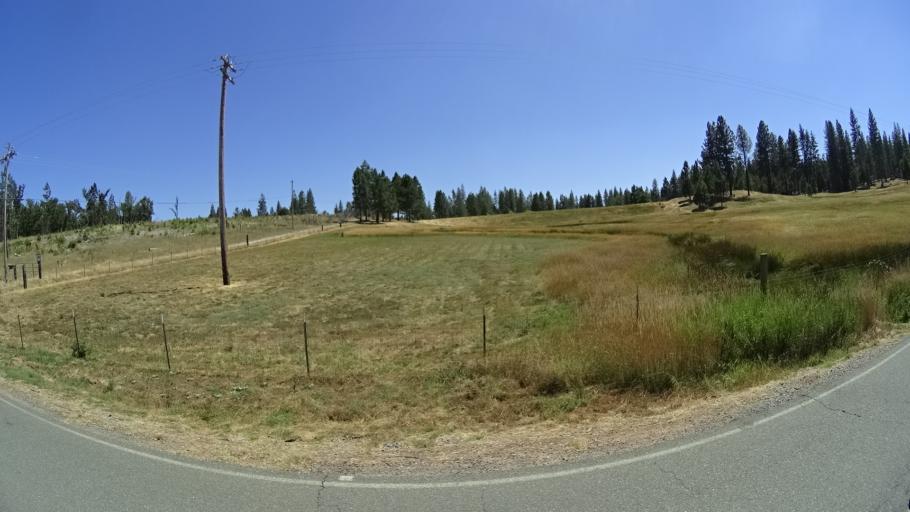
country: US
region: California
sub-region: Calaveras County
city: Mountain Ranch
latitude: 38.2843
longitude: -120.5171
